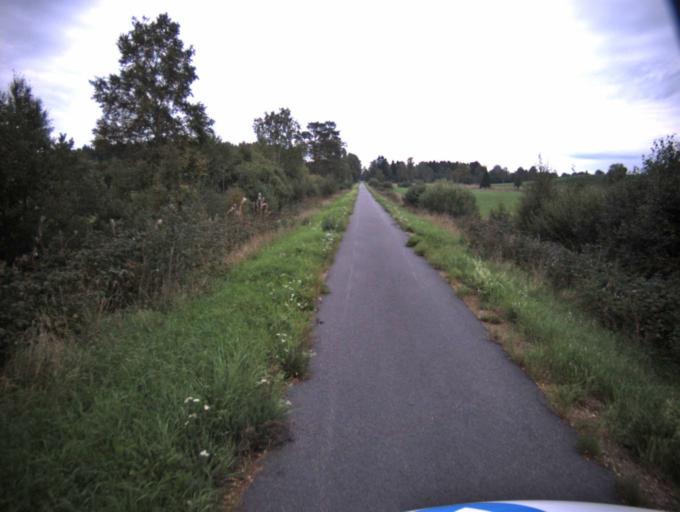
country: SE
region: Vaestra Goetaland
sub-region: Falkopings Kommun
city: Falkoeping
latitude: 58.0024
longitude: 13.5479
